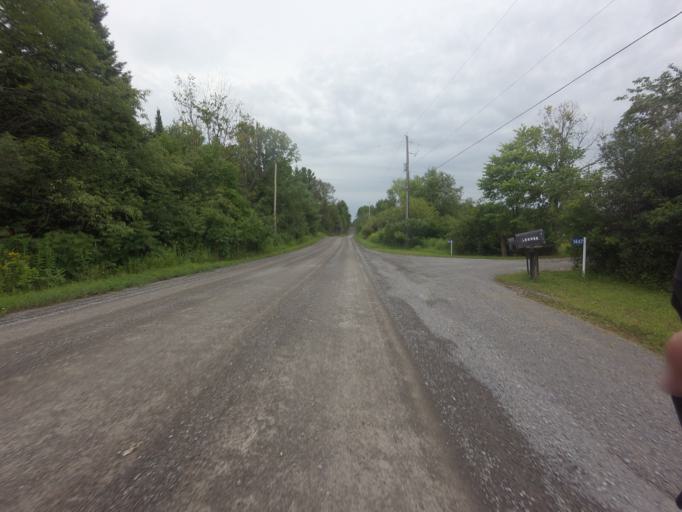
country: CA
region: Ontario
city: Carleton Place
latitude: 45.1604
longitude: -76.2685
